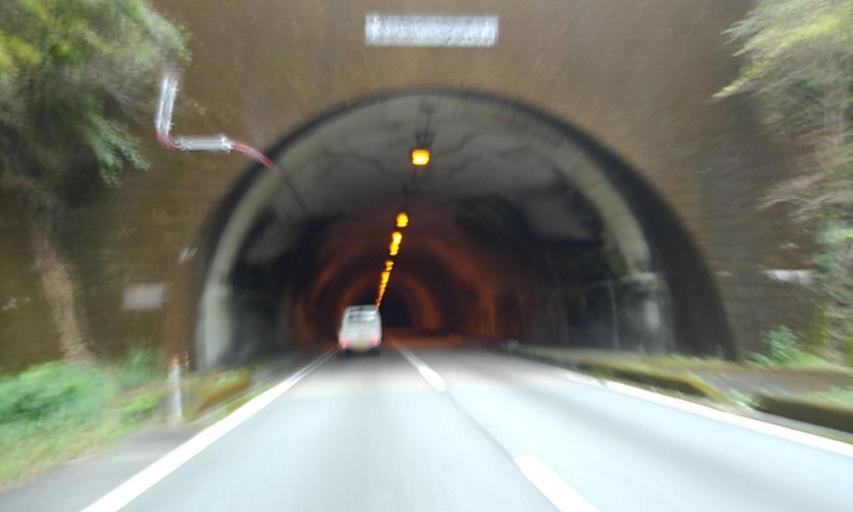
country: JP
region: Mie
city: Ise
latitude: 34.2961
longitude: 136.6202
